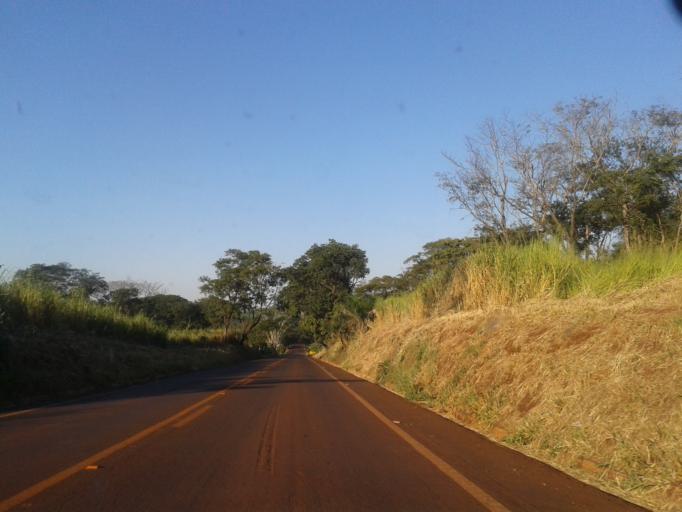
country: BR
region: Minas Gerais
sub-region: Capinopolis
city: Capinopolis
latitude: -18.6924
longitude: -49.6204
